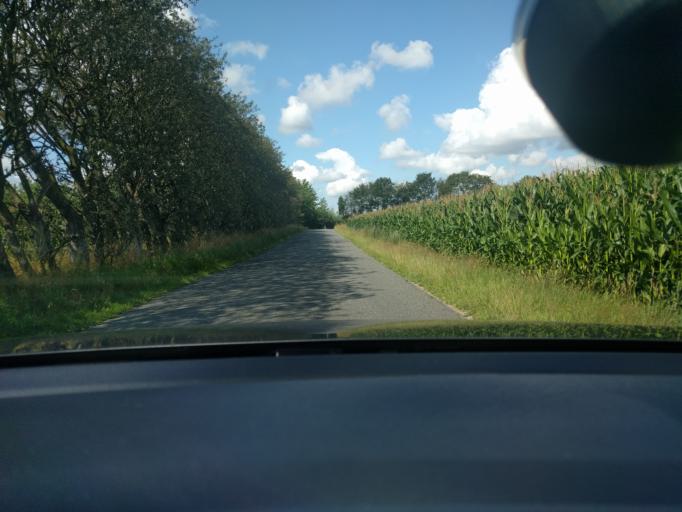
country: DK
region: Central Jutland
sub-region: Viborg Kommune
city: Viborg
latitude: 56.4406
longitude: 9.3046
